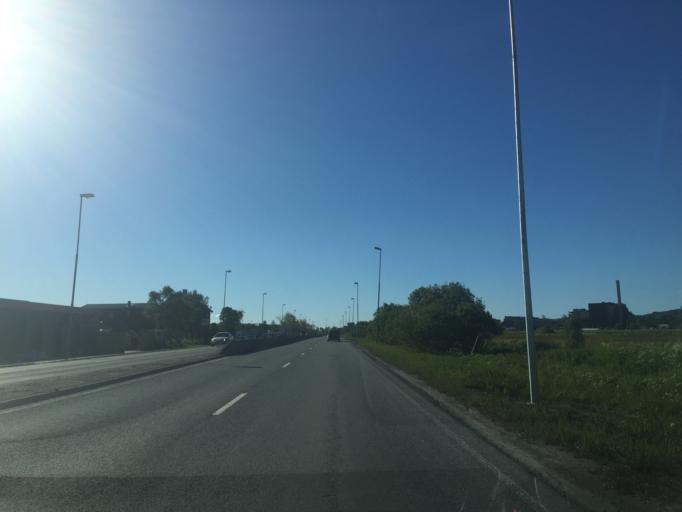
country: NO
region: Nordland
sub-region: Bodo
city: Bodo
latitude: 67.2786
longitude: 14.4311
